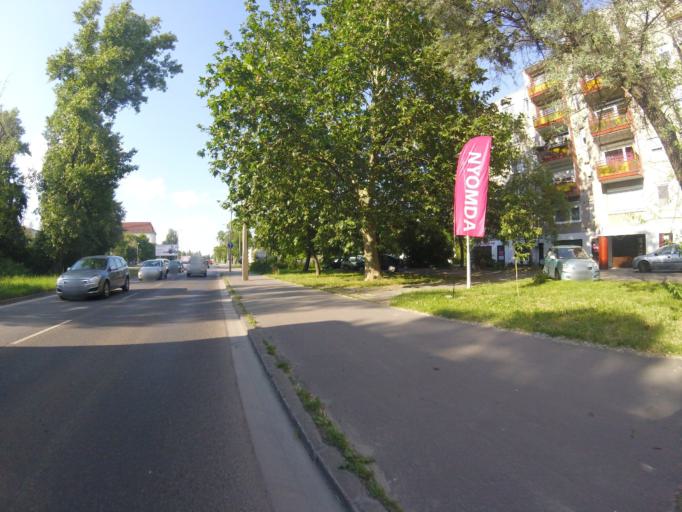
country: HU
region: Budapest
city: Budapest III. keruelet
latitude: 47.5537
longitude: 19.0404
